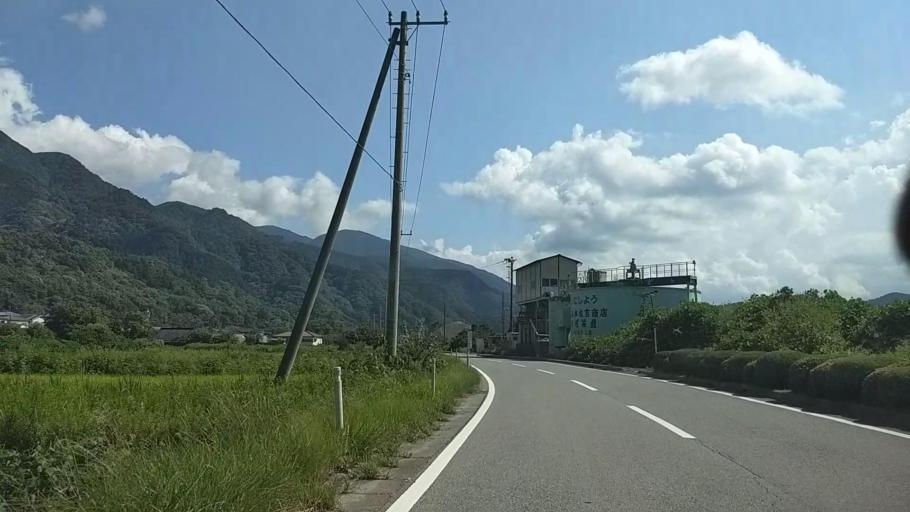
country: JP
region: Shizuoka
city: Fujinomiya
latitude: 35.3924
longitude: 138.4503
